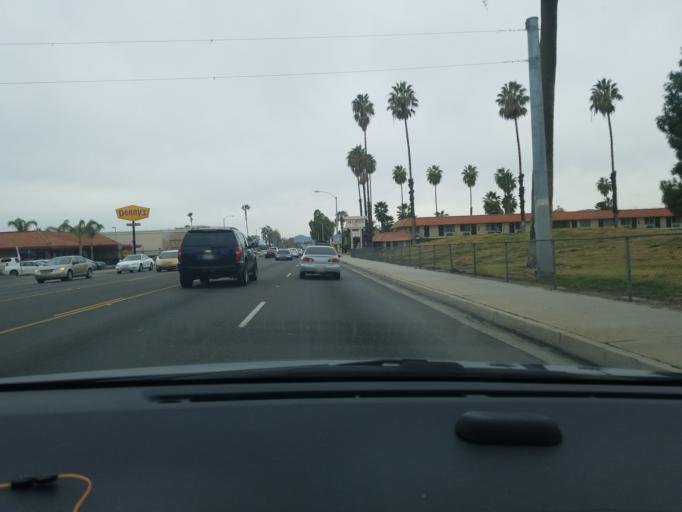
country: US
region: California
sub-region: Riverside County
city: Hemet
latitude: 33.7475
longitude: -116.9991
